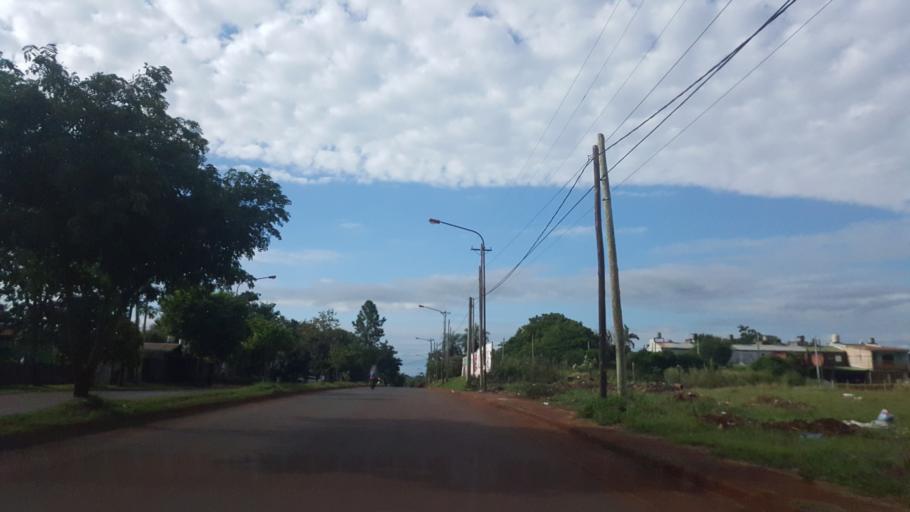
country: AR
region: Misiones
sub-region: Departamento de Capital
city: Posadas
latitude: -27.3865
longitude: -55.9345
